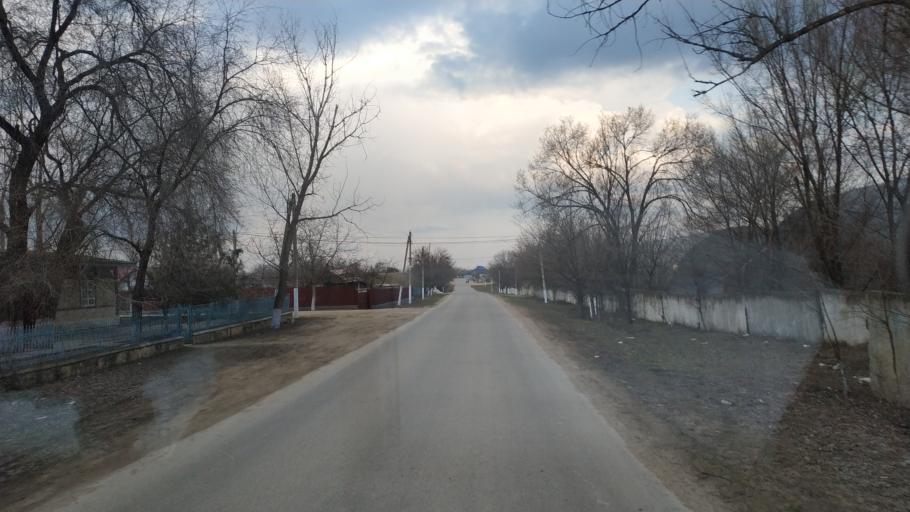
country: MD
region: Telenesti
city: Grigoriopol
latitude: 47.0259
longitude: 29.3449
